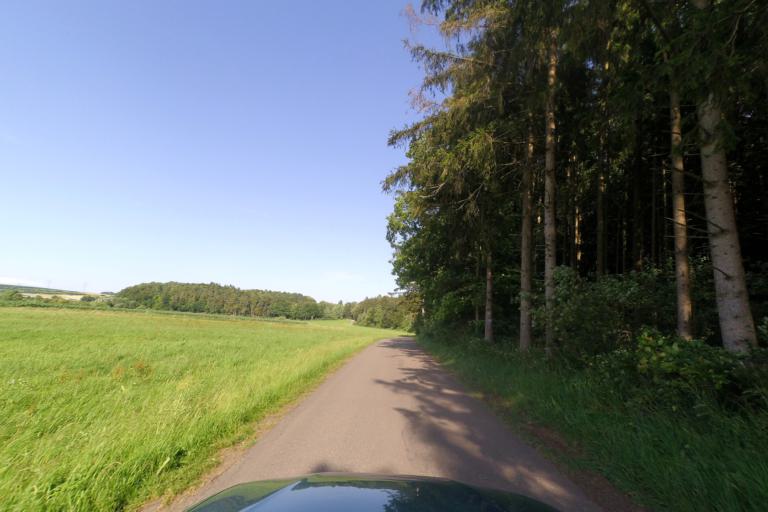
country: DE
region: Baden-Wuerttemberg
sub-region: Regierungsbezirk Stuttgart
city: Hermaringen
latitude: 48.5829
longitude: 10.2581
